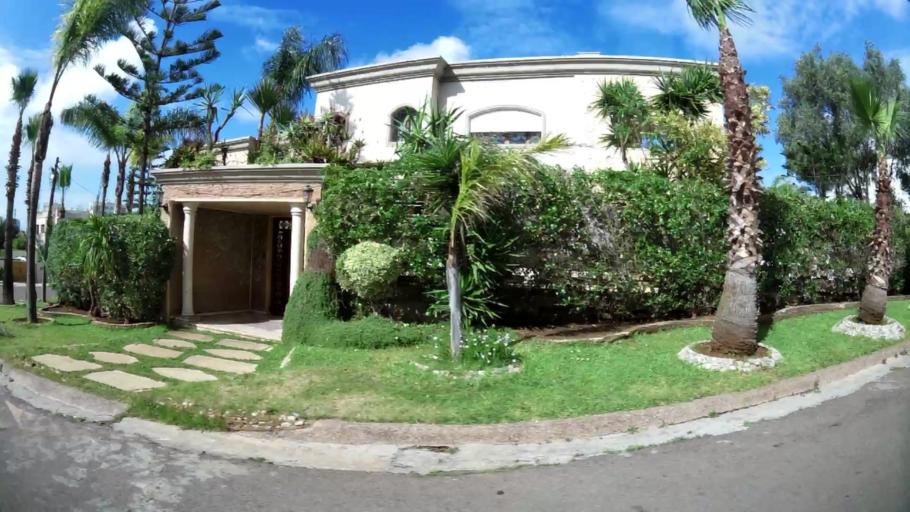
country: MA
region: Grand Casablanca
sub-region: Casablanca
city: Casablanca
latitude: 33.5500
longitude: -7.6295
